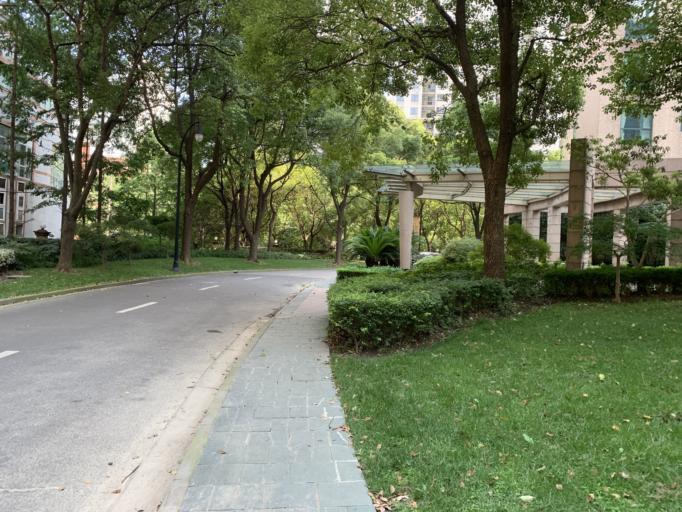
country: CN
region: Shanghai Shi
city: Pudong
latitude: 31.2315
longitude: 121.5054
